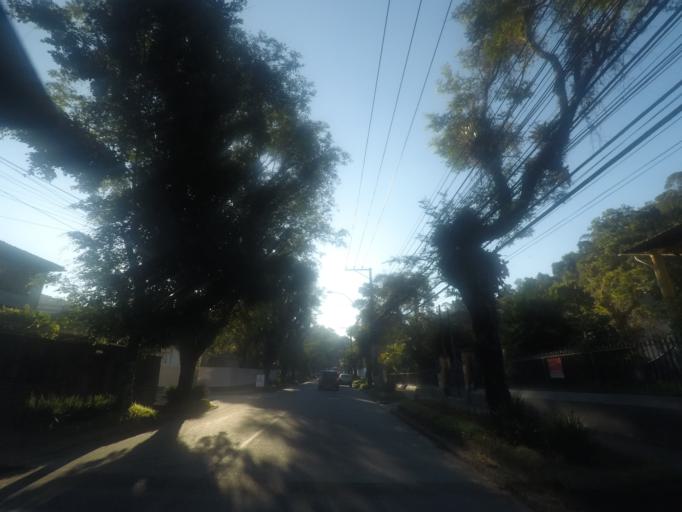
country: BR
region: Rio de Janeiro
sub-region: Petropolis
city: Petropolis
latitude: -22.5278
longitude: -43.1753
